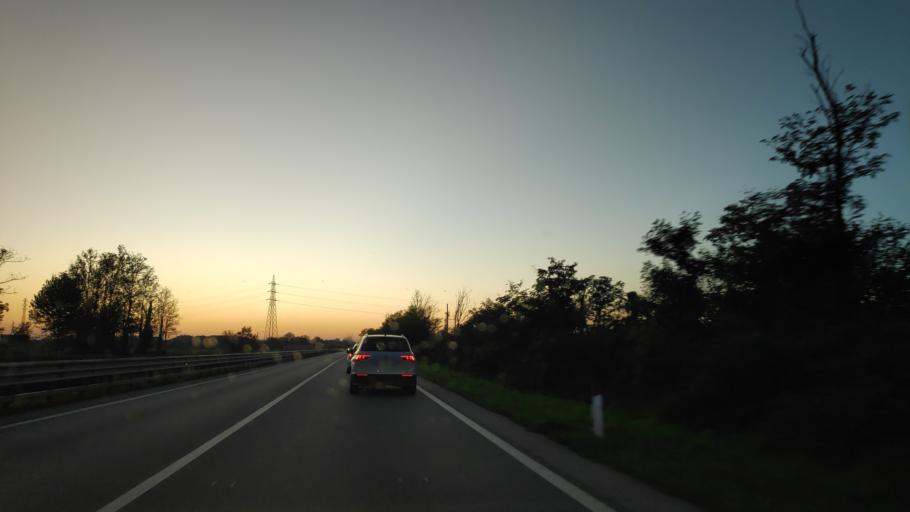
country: IT
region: Lombardy
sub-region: Citta metropolitana di Milano
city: Albairate
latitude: 45.4010
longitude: 8.9487
